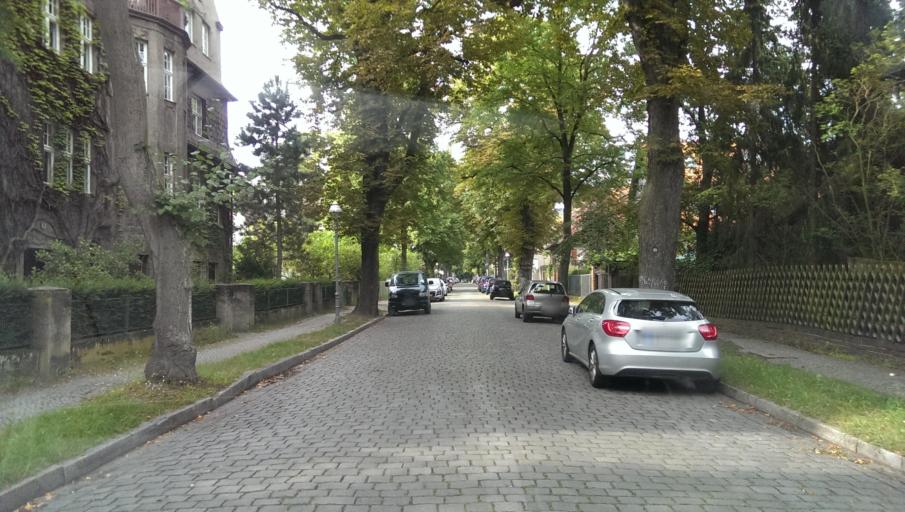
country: DE
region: Berlin
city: Zehlendorf Bezirk
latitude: 52.4322
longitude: 13.2516
